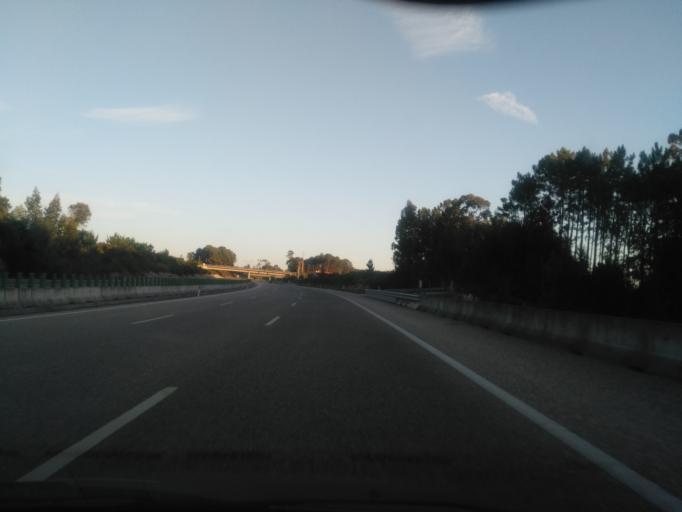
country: PT
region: Leiria
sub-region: Pombal
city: Lourical
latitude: 39.9699
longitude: -8.7815
